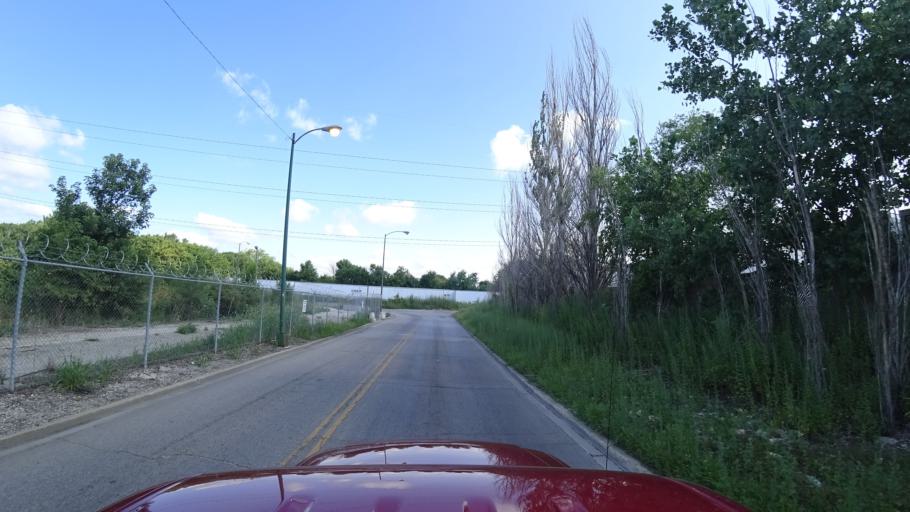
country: US
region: Illinois
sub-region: Cook County
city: Cicero
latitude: 41.8322
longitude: -87.7193
